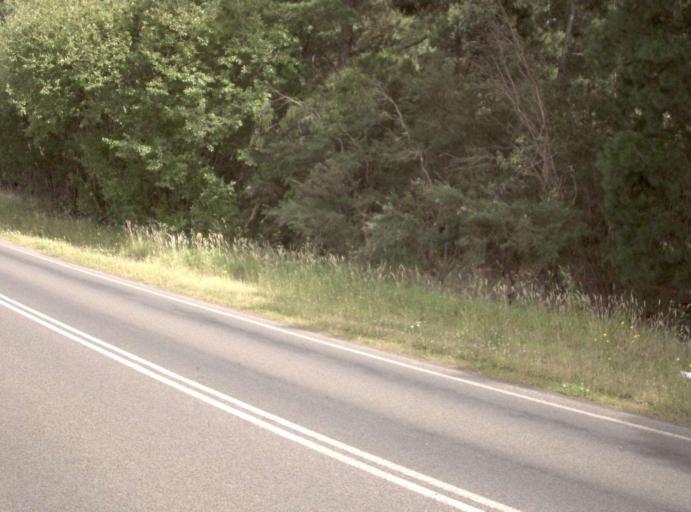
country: AU
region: Victoria
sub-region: Latrobe
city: Morwell
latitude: -38.1998
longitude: 146.4351
